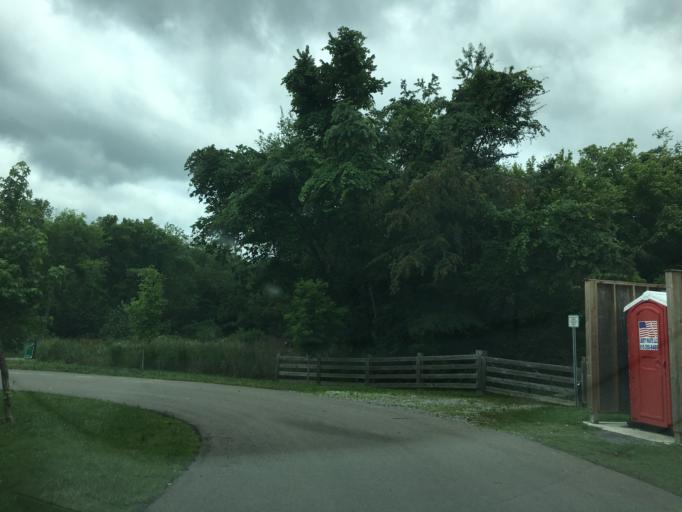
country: US
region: Tennessee
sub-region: Davidson County
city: Belle Meade
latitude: 36.0626
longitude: -86.9065
